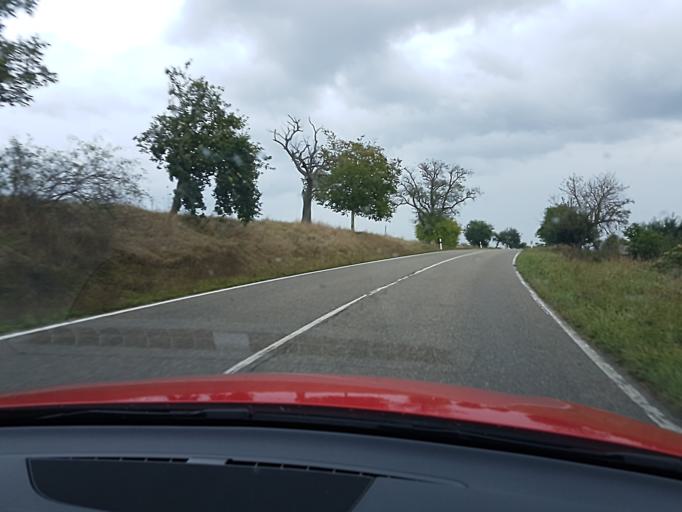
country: DE
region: Baden-Wuerttemberg
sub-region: Karlsruhe Region
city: Muhlacker
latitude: 48.9801
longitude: 8.8488
